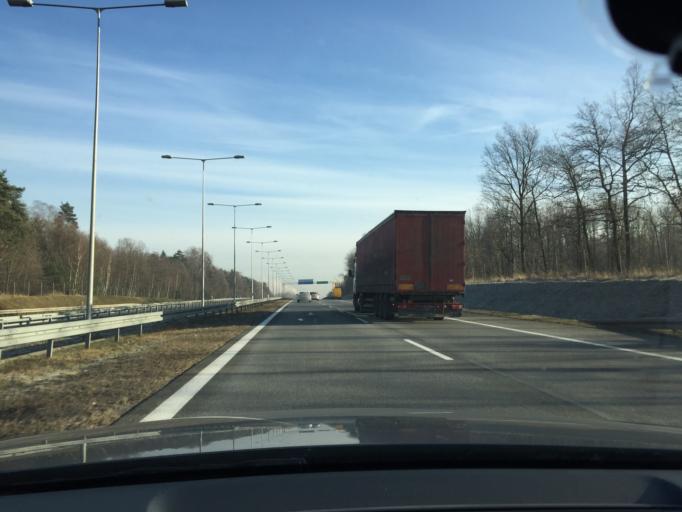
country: PL
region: Silesian Voivodeship
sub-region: Myslowice
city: Myslowice
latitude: 50.2182
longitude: 19.1156
